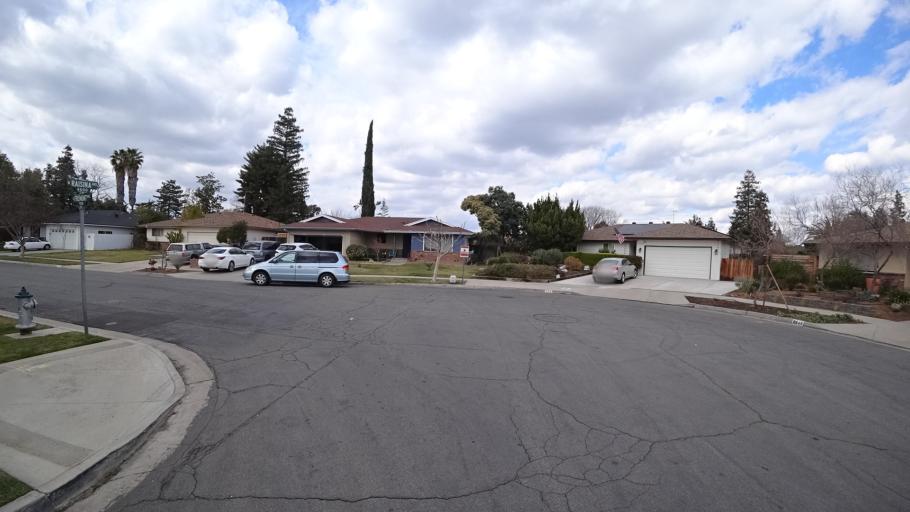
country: US
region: California
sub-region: Fresno County
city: Clovis
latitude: 36.8348
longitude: -119.7735
